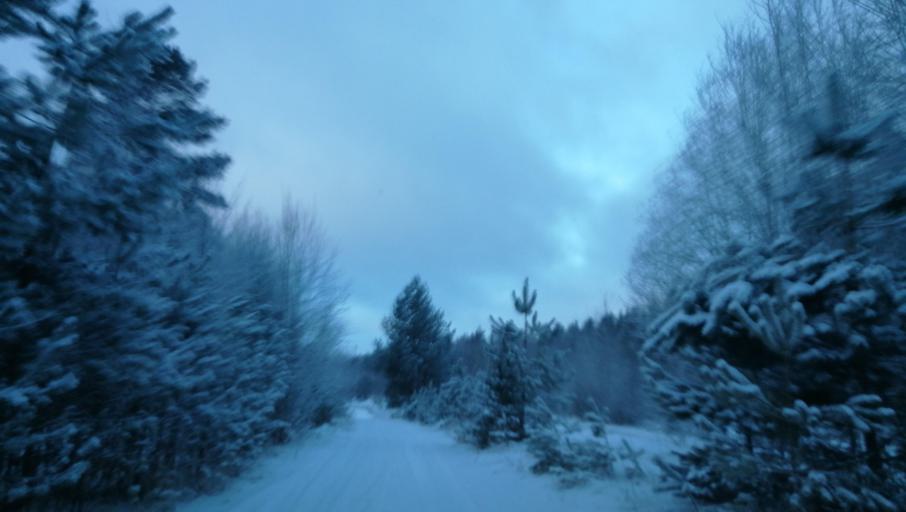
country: LV
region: Amatas Novads
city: Drabesi
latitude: 57.2080
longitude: 25.3169
